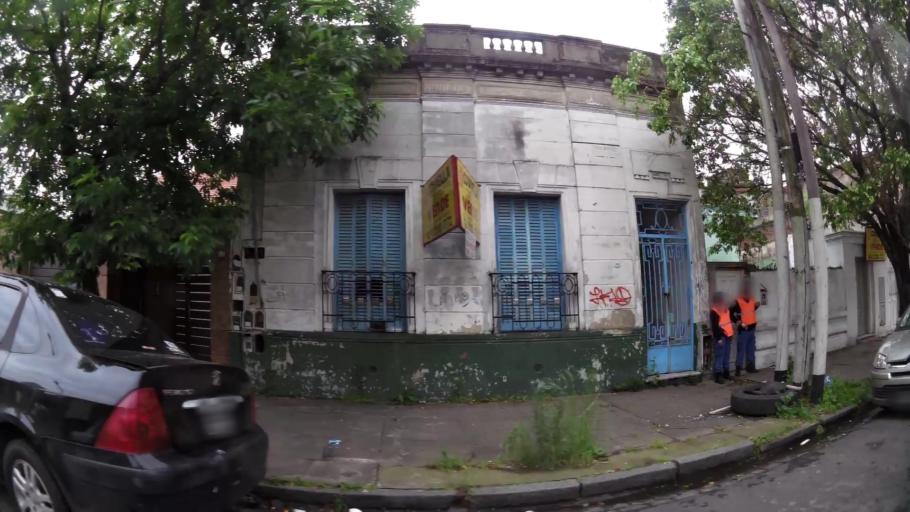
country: AR
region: Buenos Aires
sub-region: Partido de Lanus
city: Lanus
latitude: -34.7018
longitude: -58.3838
